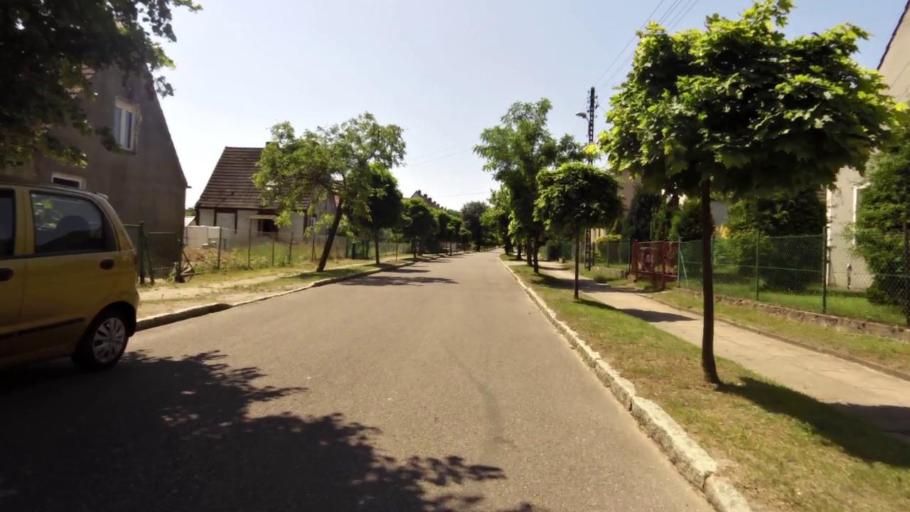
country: PL
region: West Pomeranian Voivodeship
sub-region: Powiat swidwinski
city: Polczyn-Zdroj
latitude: 53.7730
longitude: 16.1055
